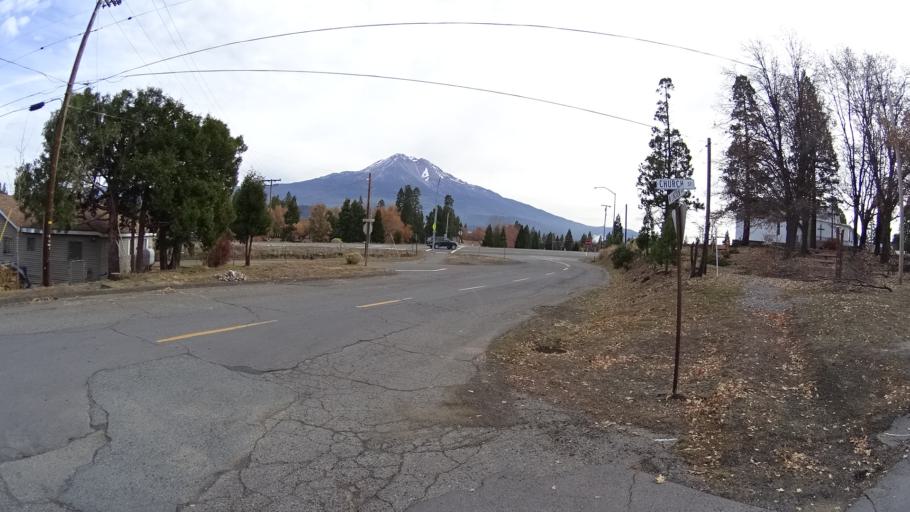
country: US
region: California
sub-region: Siskiyou County
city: Weed
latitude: 41.4369
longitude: -122.3879
